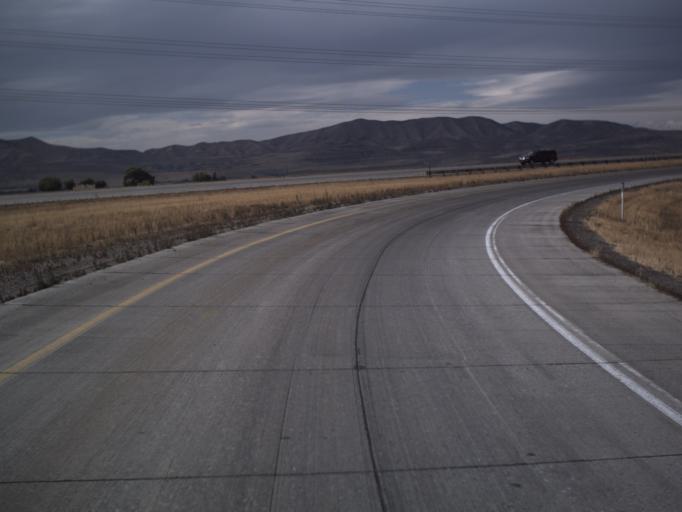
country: US
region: Utah
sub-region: Box Elder County
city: Tremonton
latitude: 41.6998
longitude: -112.1901
